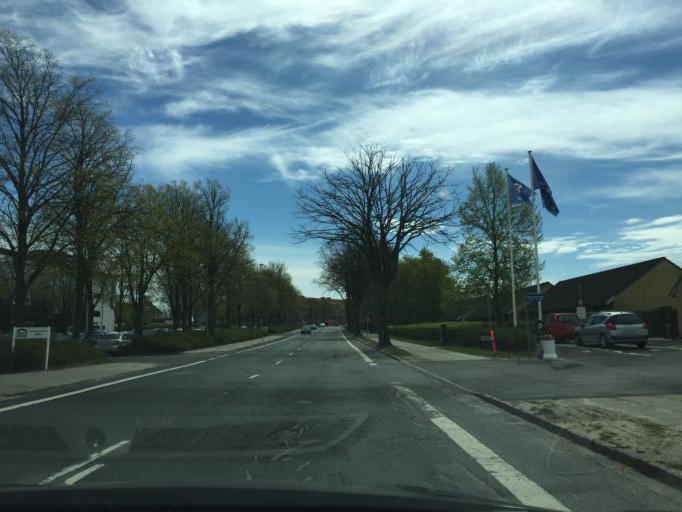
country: DK
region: South Denmark
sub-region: Odense Kommune
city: Odense
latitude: 55.3977
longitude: 10.3475
